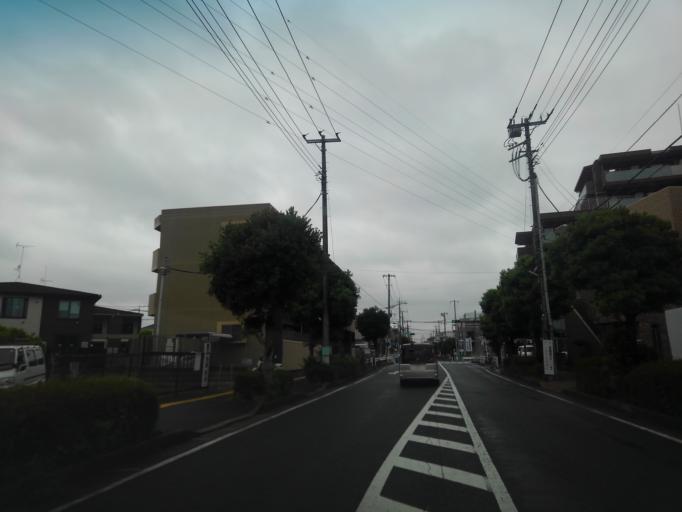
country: JP
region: Tokyo
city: Chofugaoka
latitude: 35.6610
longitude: 139.5023
